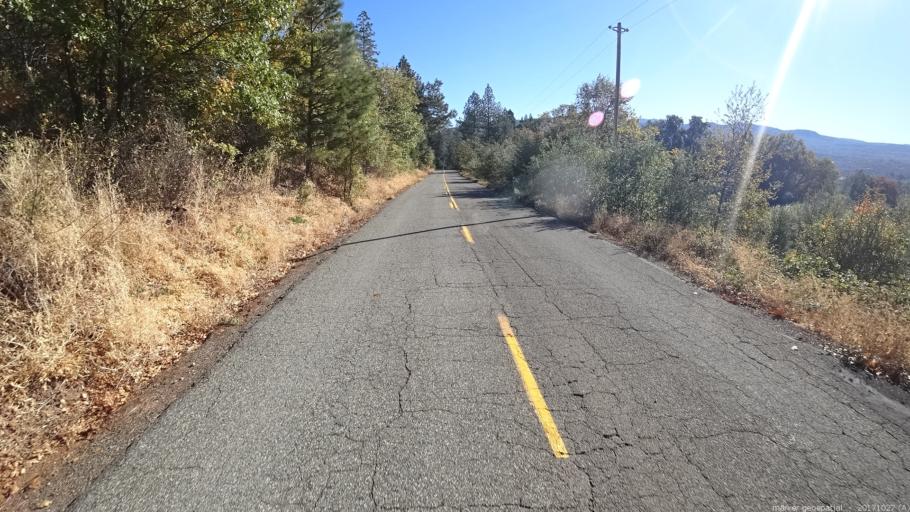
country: US
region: California
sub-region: Shasta County
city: Burney
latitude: 40.8262
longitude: -121.9433
